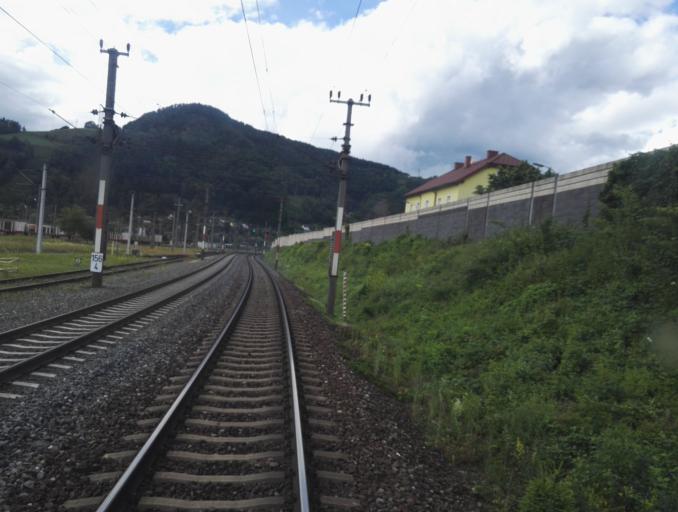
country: AT
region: Styria
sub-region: Politischer Bezirk Bruck-Muerzzuschlag
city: Bruck an der Mur
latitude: 47.4262
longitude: 15.2777
